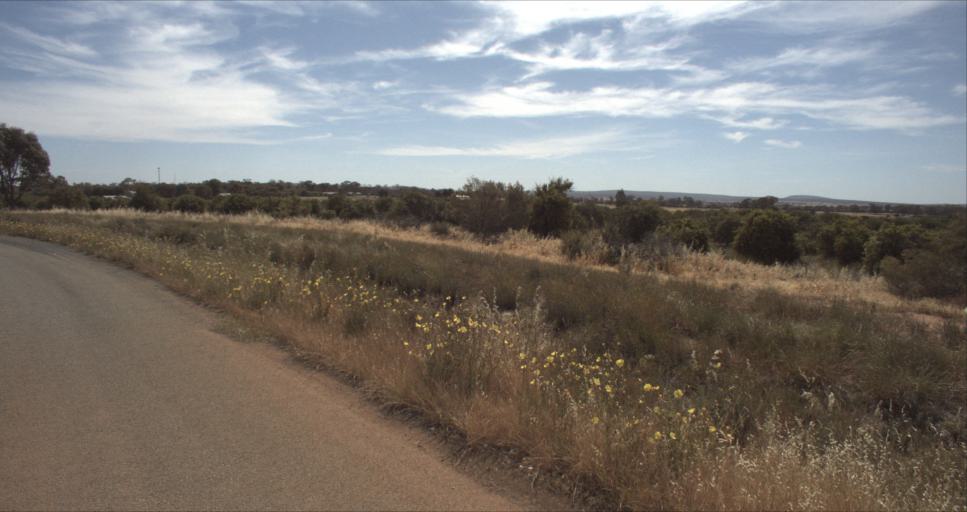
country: AU
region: New South Wales
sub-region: Leeton
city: Leeton
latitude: -34.5755
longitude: 146.4555
